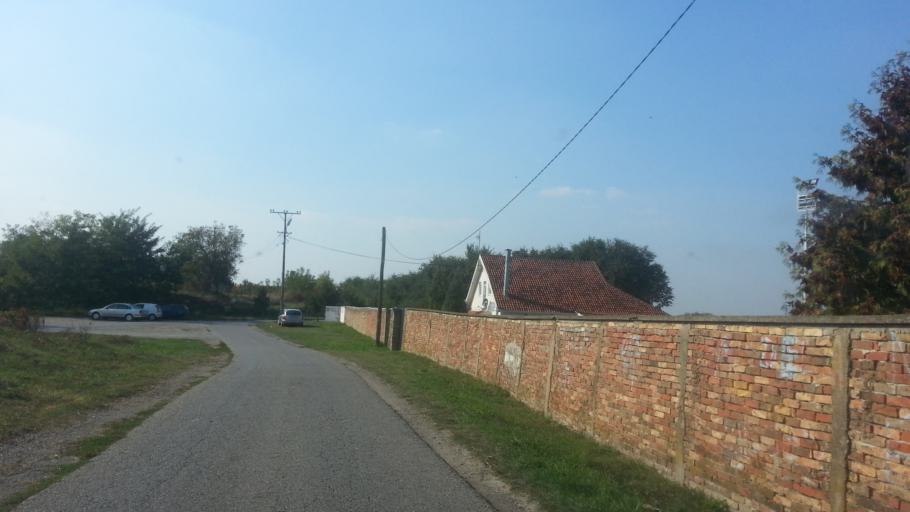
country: RS
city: Stari Banovci
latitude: 44.9883
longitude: 20.2765
